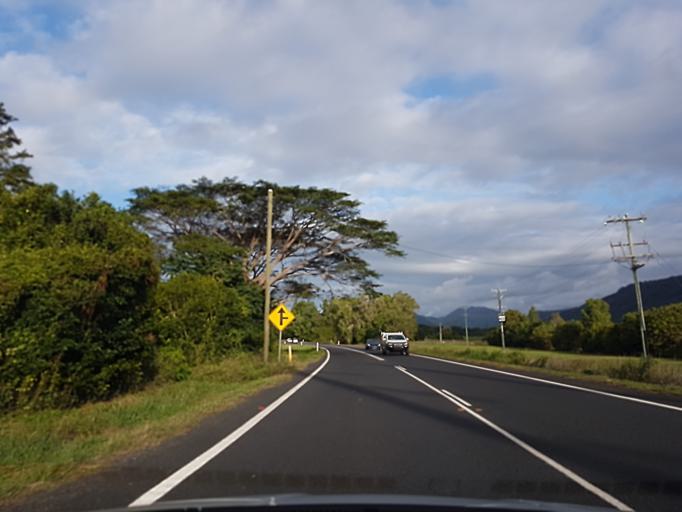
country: AU
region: Queensland
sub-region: Cairns
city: Port Douglas
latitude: -16.5203
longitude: 145.4504
